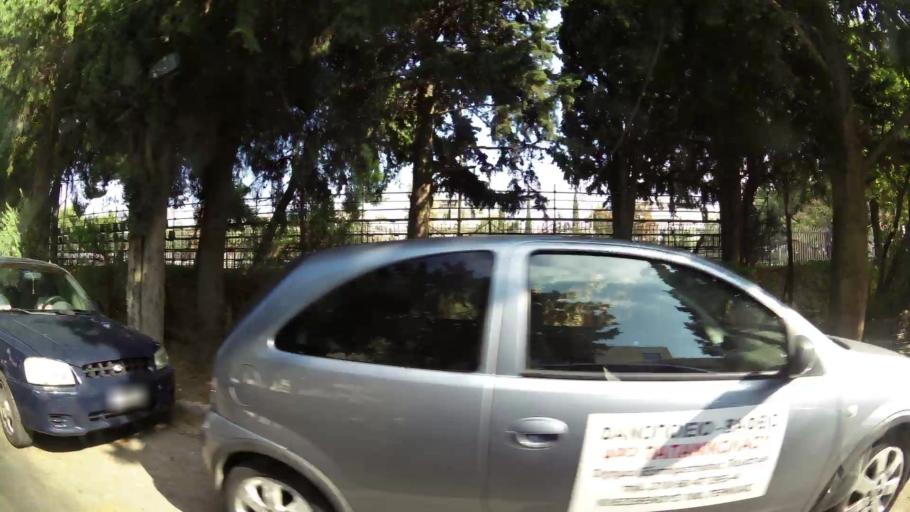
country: GR
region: Attica
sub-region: Nomarchia Athinas
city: Neo Psychiko
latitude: 37.9960
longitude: 23.7866
